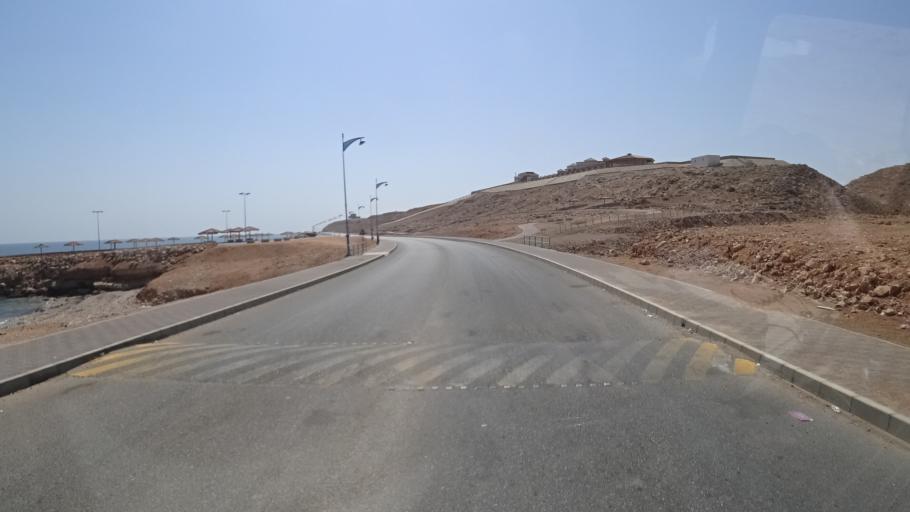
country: OM
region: Ash Sharqiyah
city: Sur
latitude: 22.5667
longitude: 59.5574
